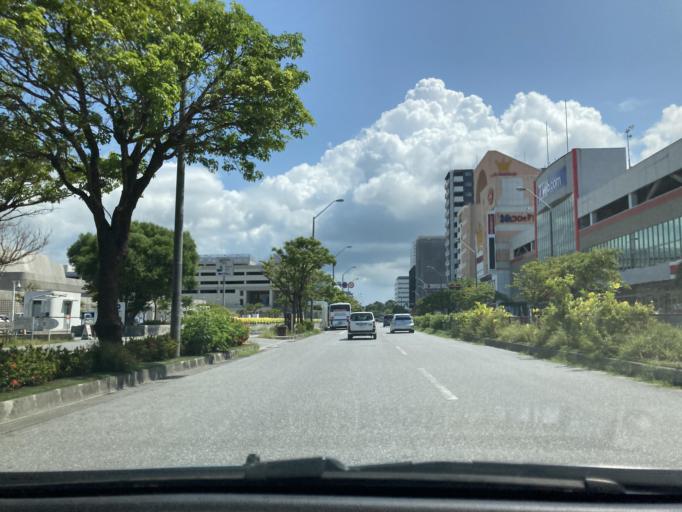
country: JP
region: Okinawa
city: Naha-shi
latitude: 26.2273
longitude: 127.6922
